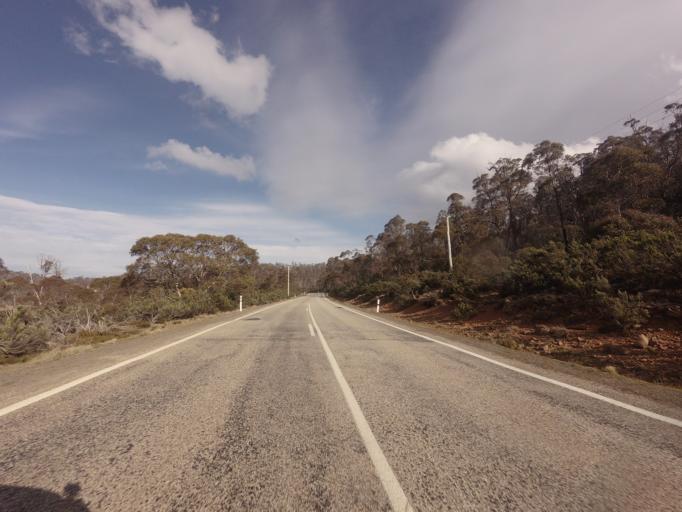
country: AU
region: Tasmania
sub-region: Meander Valley
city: Deloraine
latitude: -41.9846
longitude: 146.6794
